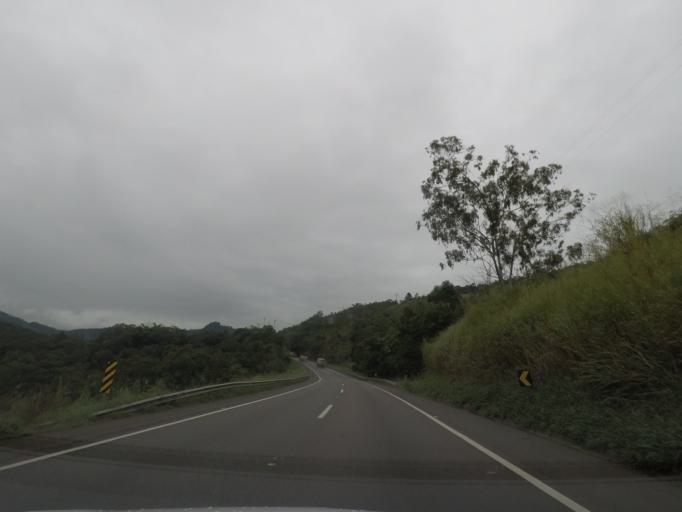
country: BR
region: Sao Paulo
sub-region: Cajati
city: Cajati
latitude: -24.7871
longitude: -48.2034
